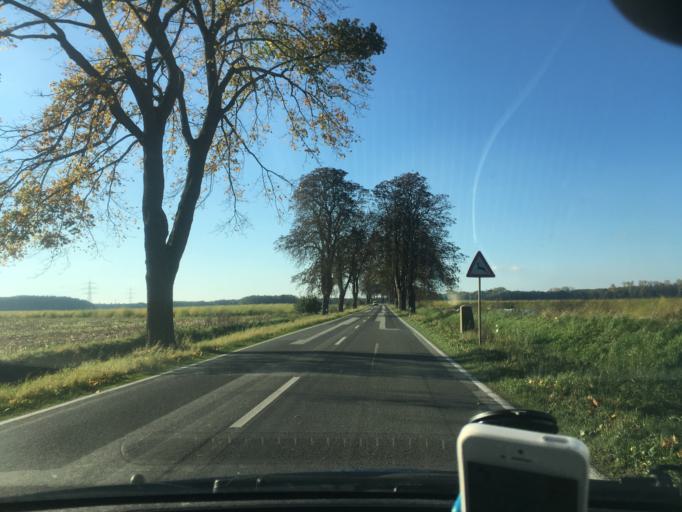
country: DE
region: Mecklenburg-Vorpommern
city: Wittenburg
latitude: 53.5202
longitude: 11.0038
